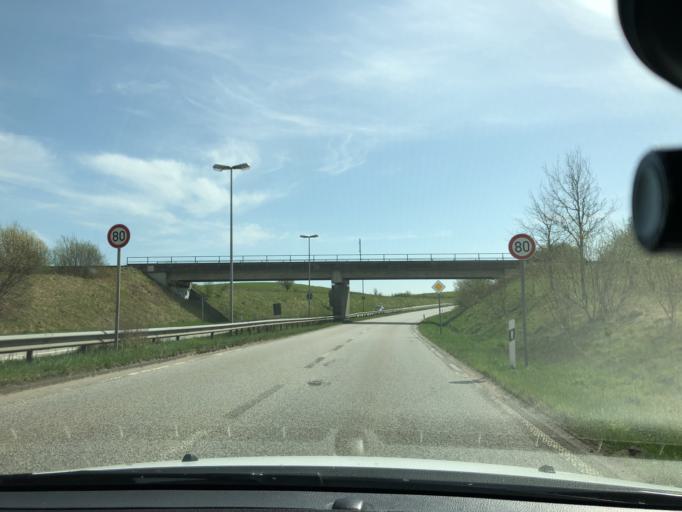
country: DE
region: Schleswig-Holstein
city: Tastrup
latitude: 54.7704
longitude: 9.4603
